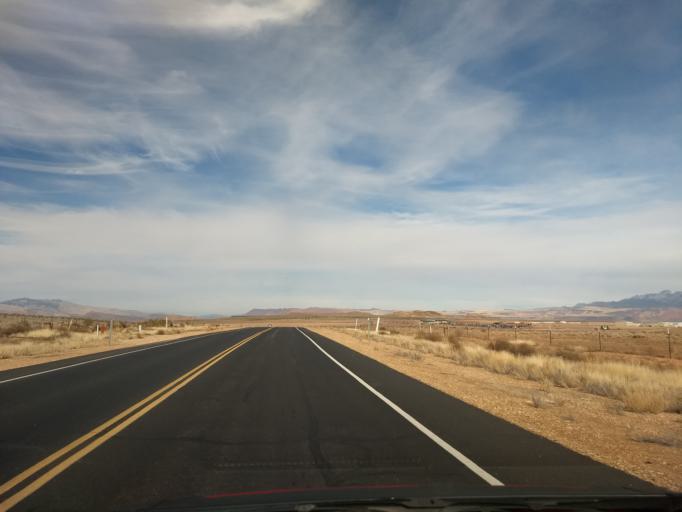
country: US
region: Utah
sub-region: Washington County
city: Washington
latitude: 37.0207
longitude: -113.5030
